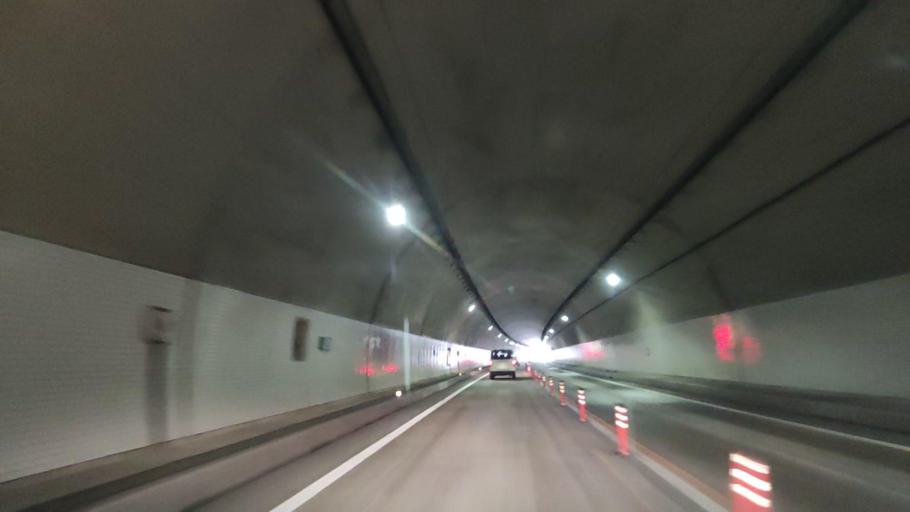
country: JP
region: Akita
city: Odate
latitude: 40.3307
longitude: 140.6089
